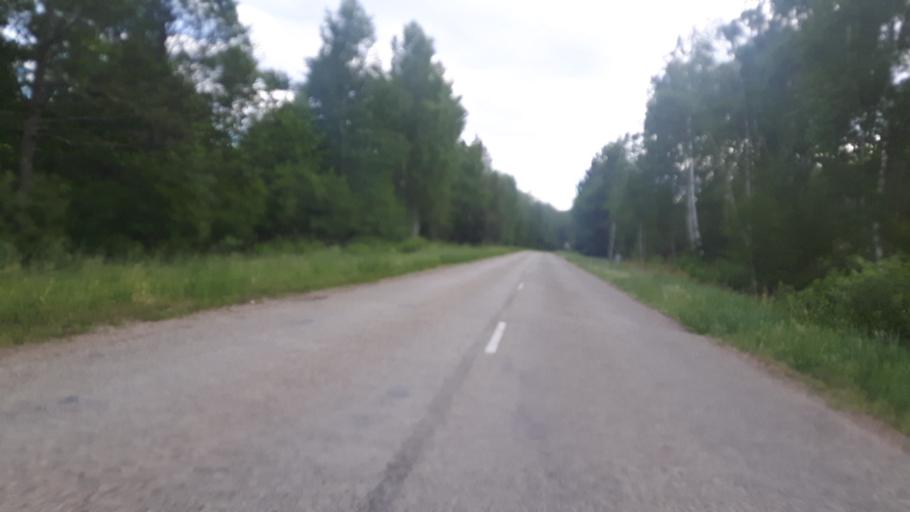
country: LV
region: Engure
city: Smarde
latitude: 57.0291
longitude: 23.3596
